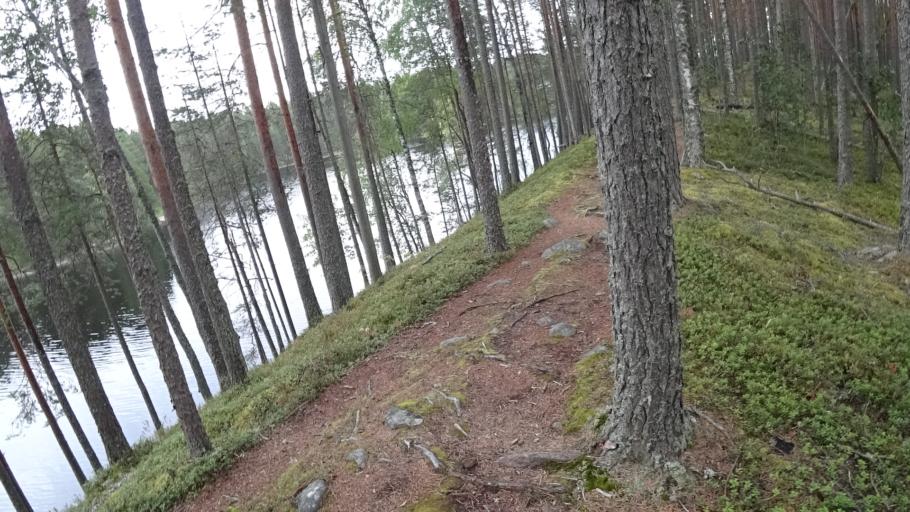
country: FI
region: North Karelia
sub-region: Joensuu
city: Ilomantsi
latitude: 62.5786
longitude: 31.1686
